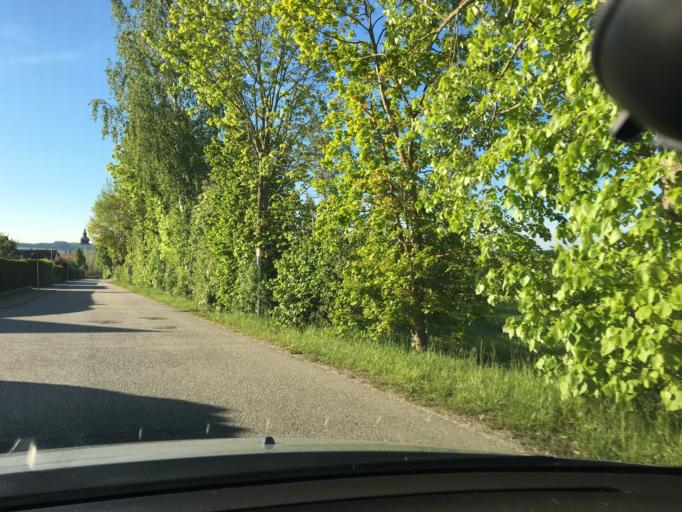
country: DE
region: Bavaria
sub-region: Lower Bavaria
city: Furth
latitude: 48.4277
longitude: 12.4051
